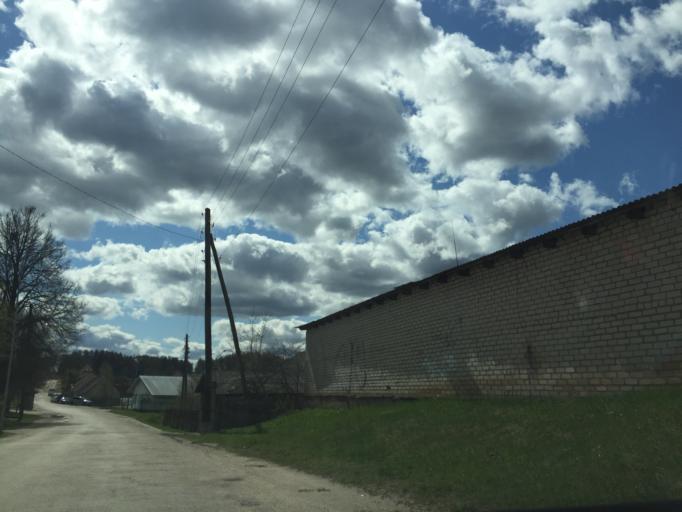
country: LV
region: Rezekne
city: Rezekne
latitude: 56.4881
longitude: 27.3419
